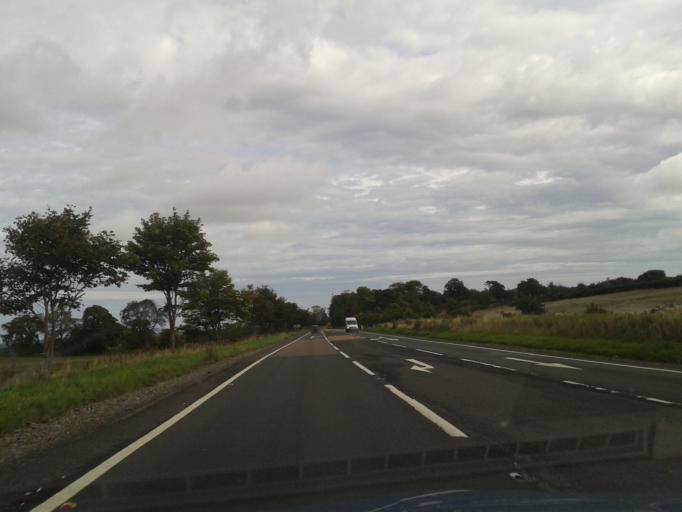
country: GB
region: Scotland
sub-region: Moray
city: Hopeman
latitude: 57.6471
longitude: -3.4326
